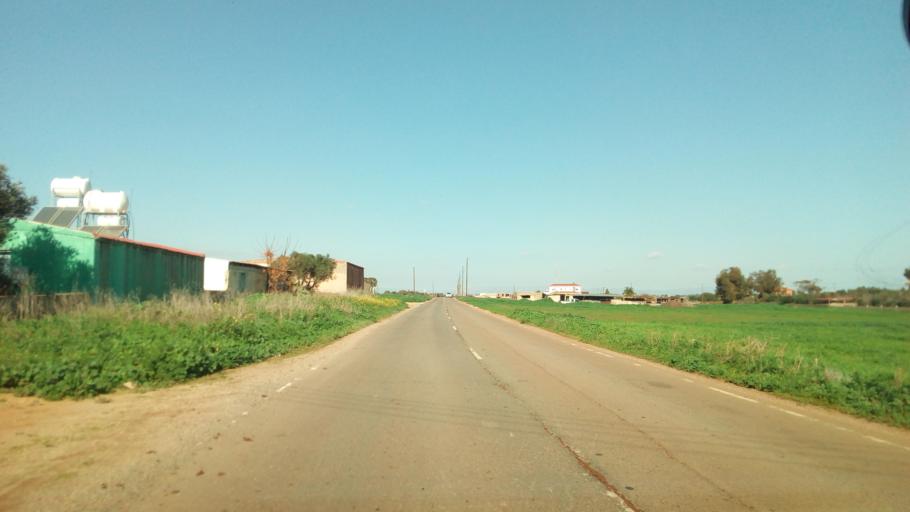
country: CY
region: Ammochostos
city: Avgorou
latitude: 34.9902
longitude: 33.8472
